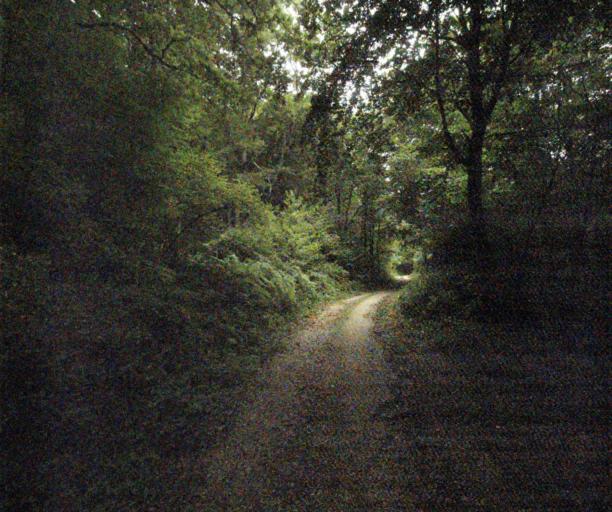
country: FR
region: Midi-Pyrenees
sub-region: Departement du Tarn
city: Soreze
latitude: 43.4180
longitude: 2.0633
